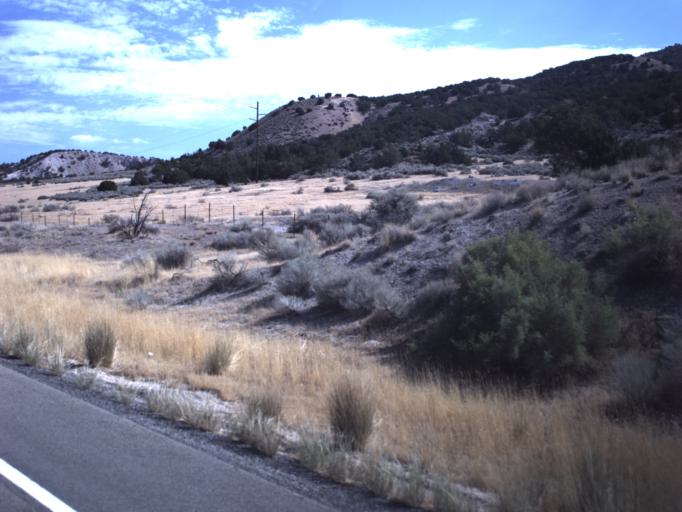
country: US
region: Utah
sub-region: Sanpete County
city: Gunnison
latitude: 39.4094
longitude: -111.9259
